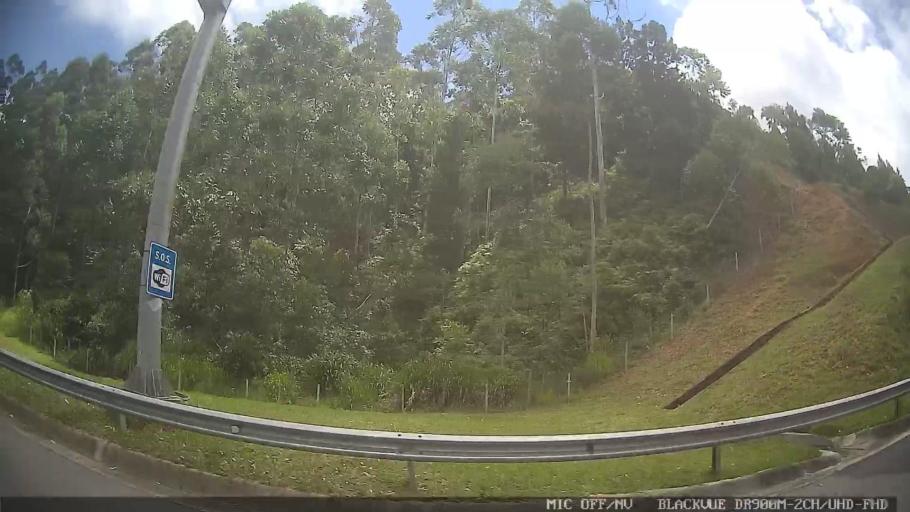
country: BR
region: Sao Paulo
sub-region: Caraguatatuba
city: Caraguatatuba
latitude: -23.5248
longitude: -45.5378
